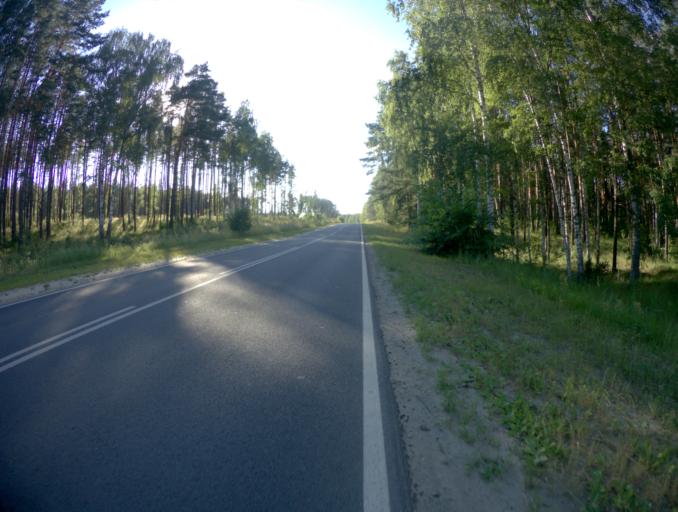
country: RU
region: Nizjnij Novgorod
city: Taremskoye
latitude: 56.0085
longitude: 42.9829
